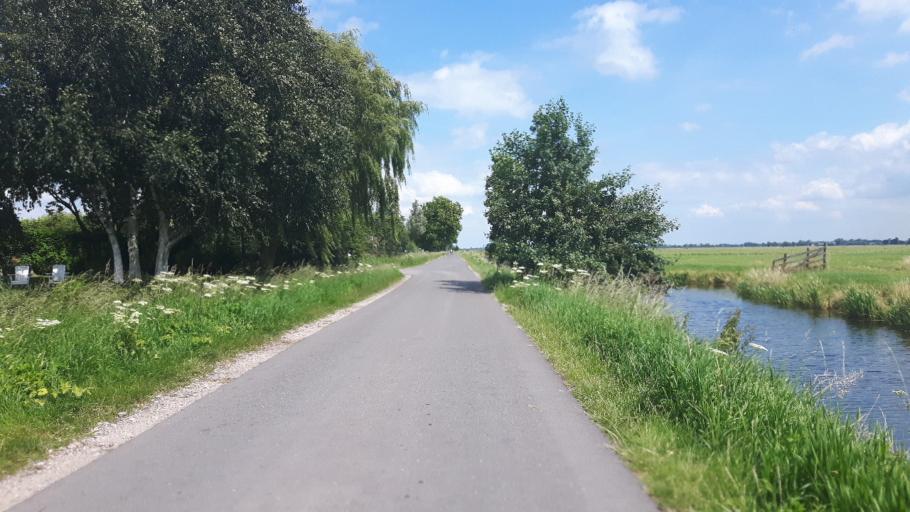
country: NL
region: South Holland
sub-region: Molenwaard
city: Nieuw-Lekkerland
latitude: 51.9106
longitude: 4.6934
